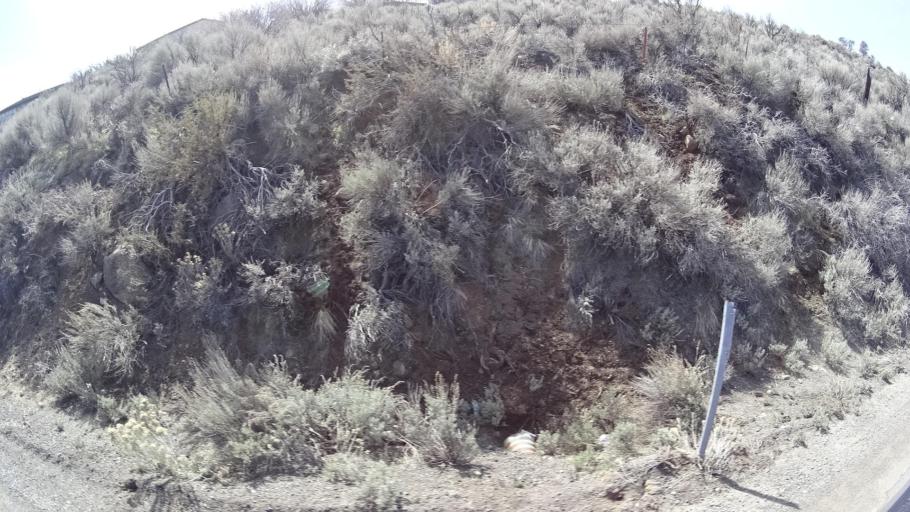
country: US
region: Nevada
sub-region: Washoe County
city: Verdi
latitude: 39.5193
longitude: -119.9813
